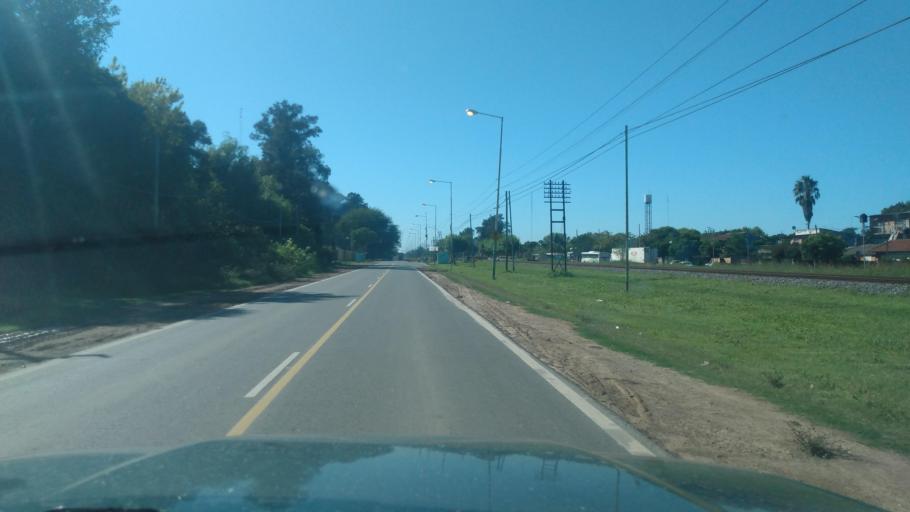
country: AR
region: Buenos Aires
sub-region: Partido de General Rodriguez
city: General Rodriguez
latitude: -34.5977
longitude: -59.0001
